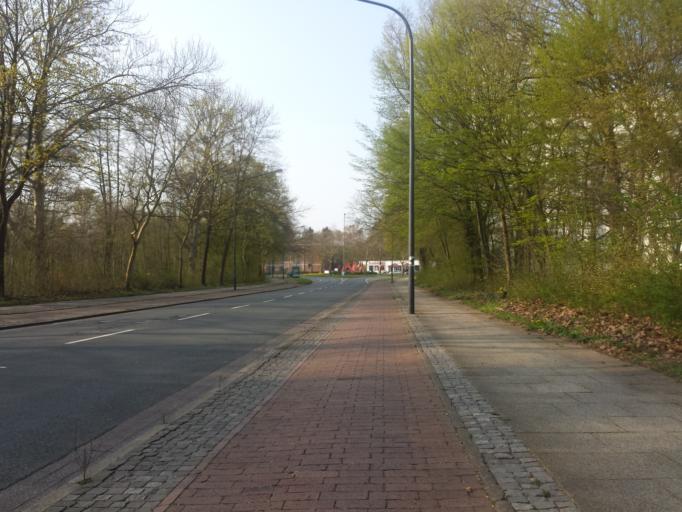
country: DE
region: Lower Saxony
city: Lilienthal
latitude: 53.0846
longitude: 8.8900
